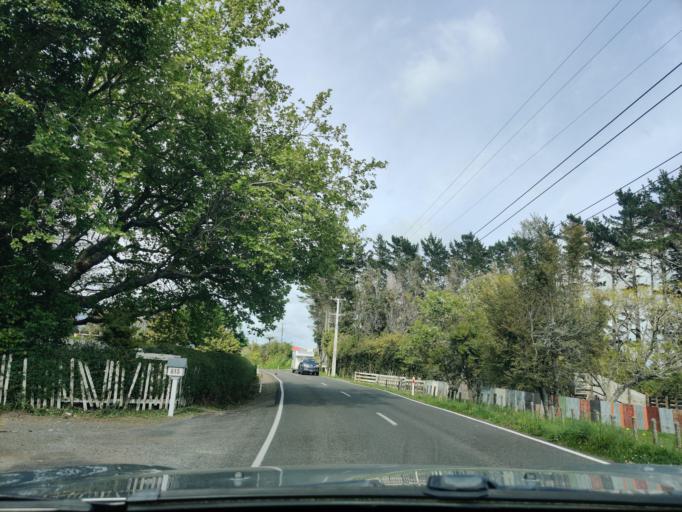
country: NZ
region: Taranaki
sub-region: New Plymouth District
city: New Plymouth
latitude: -39.1170
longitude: 174.0950
